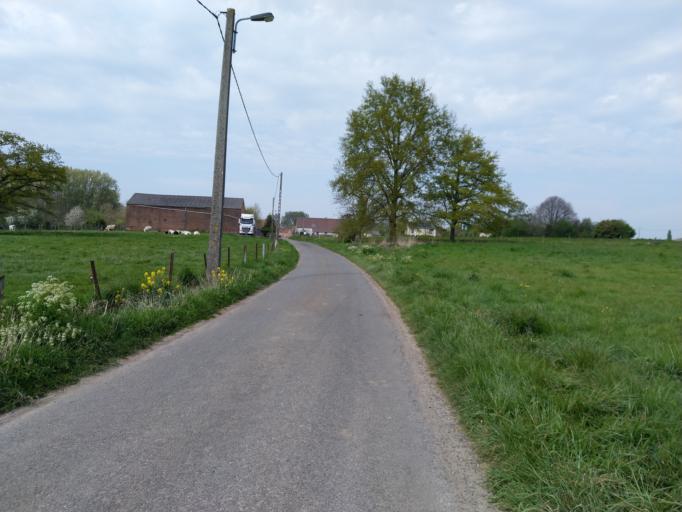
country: BE
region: Wallonia
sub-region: Province du Hainaut
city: Jurbise
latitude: 50.5273
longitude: 3.8852
